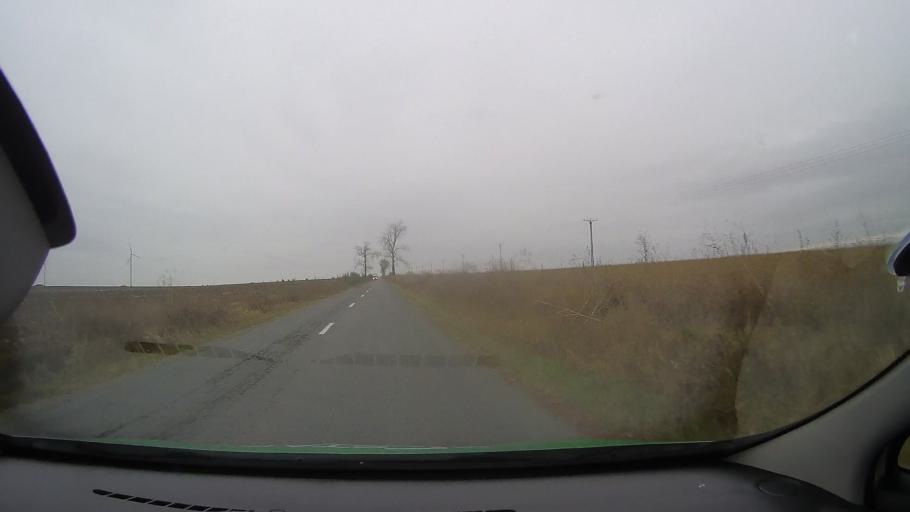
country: RO
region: Constanta
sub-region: Comuna Pantelimon
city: Pantelimon
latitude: 44.5645
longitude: 28.3192
